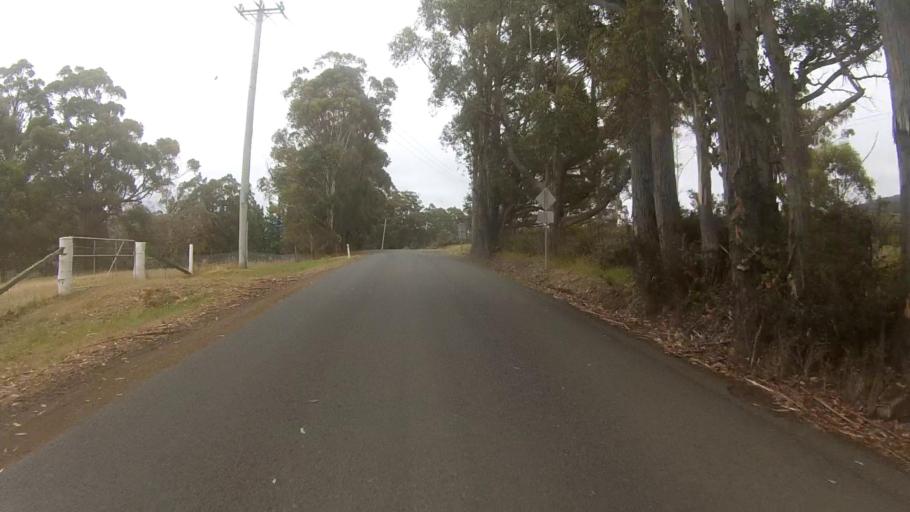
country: AU
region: Tasmania
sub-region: Kingborough
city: Margate
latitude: -42.9620
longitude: 147.2135
